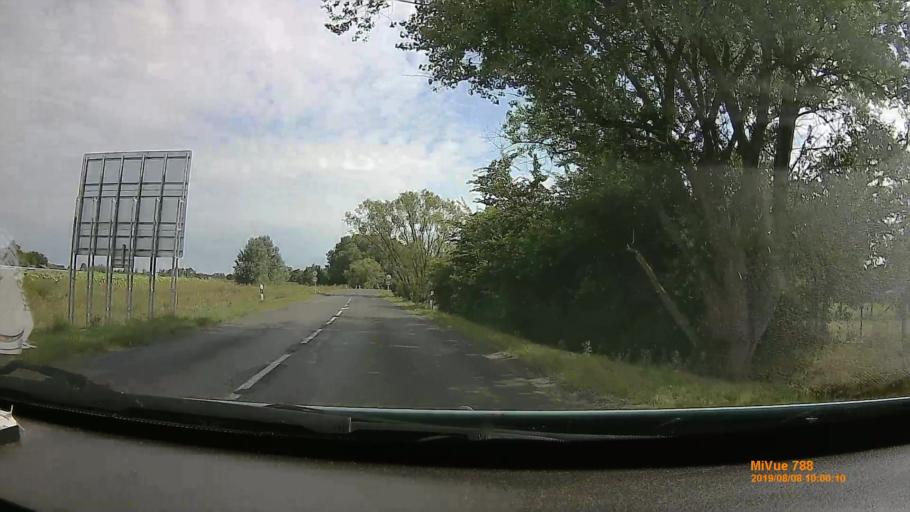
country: HU
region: Hajdu-Bihar
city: Hajdusamson
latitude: 47.5877
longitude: 21.7259
